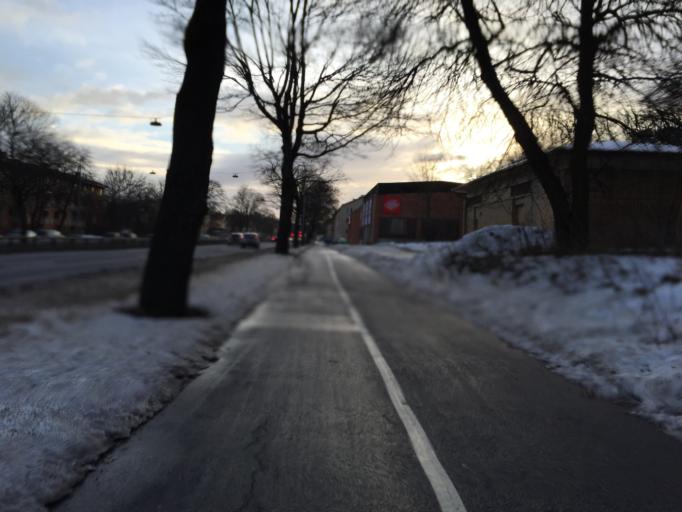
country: SE
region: Stockholm
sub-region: Stockholms Kommun
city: Bromma
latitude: 59.3383
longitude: 17.9471
